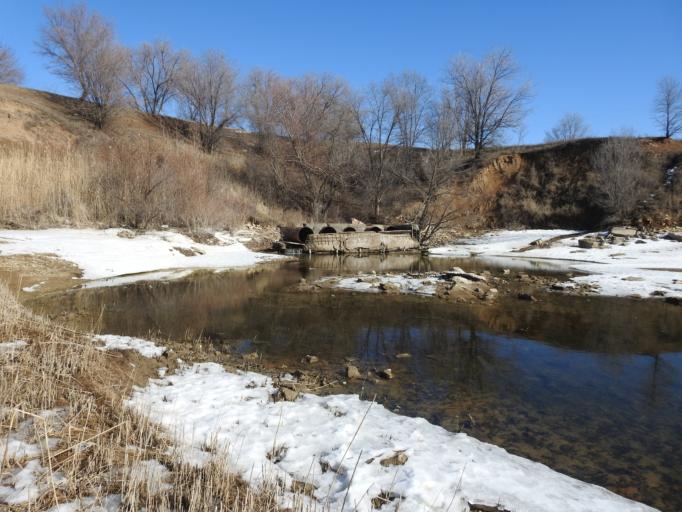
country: RU
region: Saratov
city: Yershov
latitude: 51.3727
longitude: 48.2394
